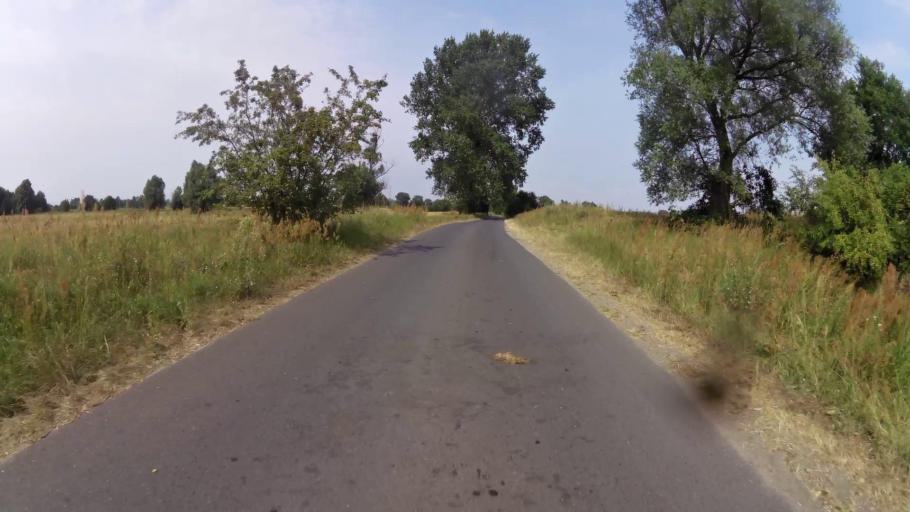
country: PL
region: West Pomeranian Voivodeship
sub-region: Powiat mysliborski
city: Nowogrodek Pomorski
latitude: 52.9685
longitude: 15.0220
